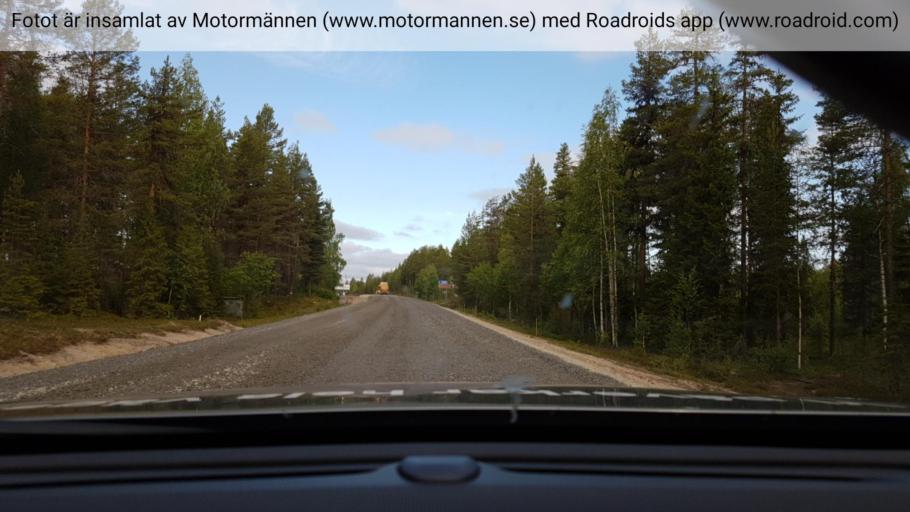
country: SE
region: Vaesterbotten
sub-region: Norsjo Kommun
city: Norsjoe
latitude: 64.6817
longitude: 19.2427
